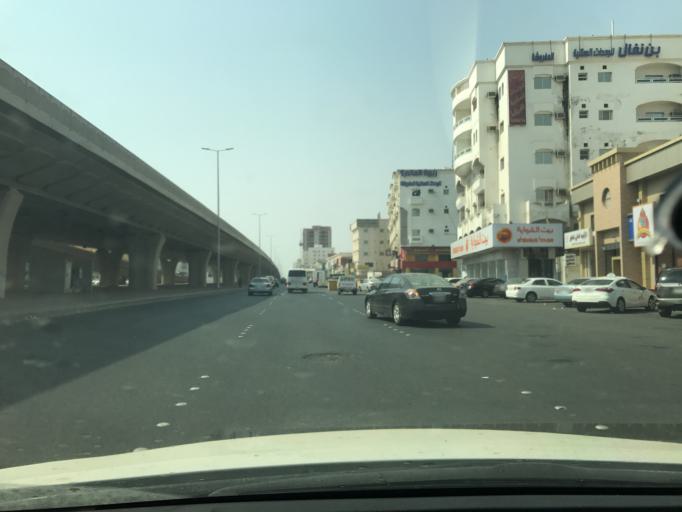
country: SA
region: Makkah
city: Jeddah
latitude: 21.6168
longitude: 39.1669
